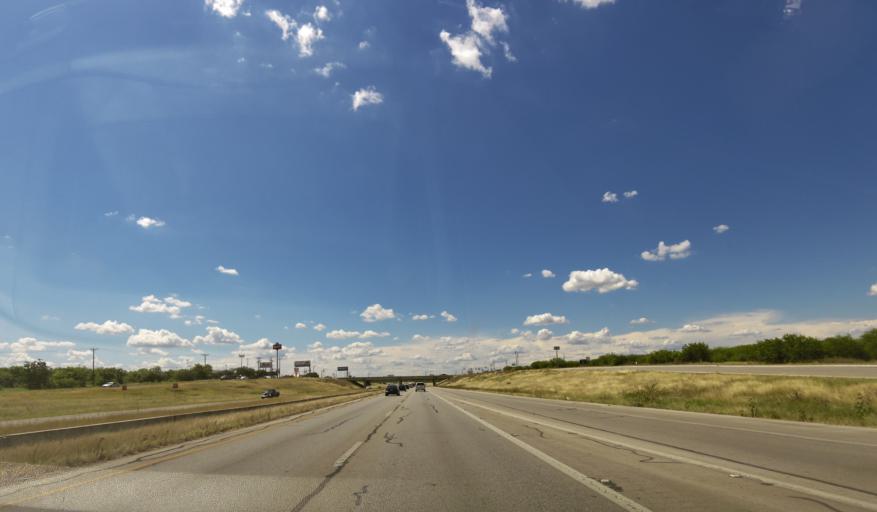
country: US
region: Texas
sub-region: Bexar County
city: Live Oak
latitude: 29.5892
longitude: -98.3500
